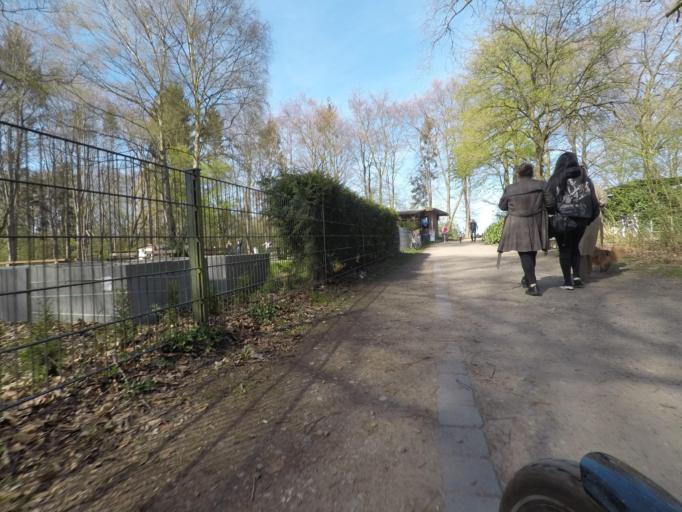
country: DE
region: Schleswig-Holstein
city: Oststeinbek
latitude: 53.5519
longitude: 10.1348
